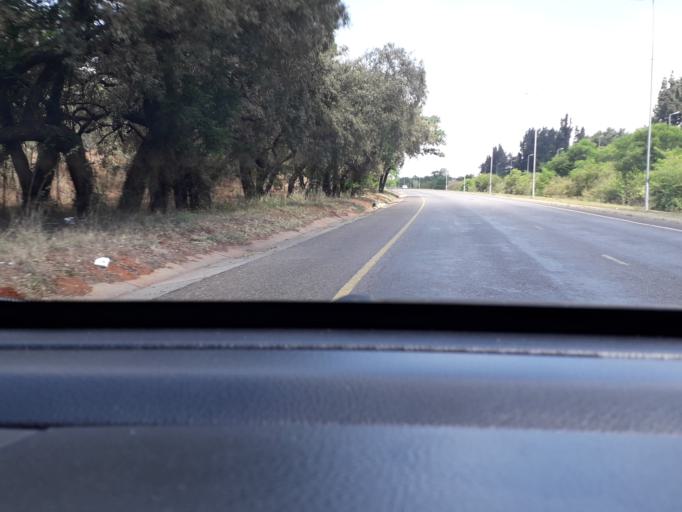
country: ZA
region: Gauteng
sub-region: City of Tshwane Metropolitan Municipality
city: Pretoria
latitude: -25.7973
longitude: 28.1967
